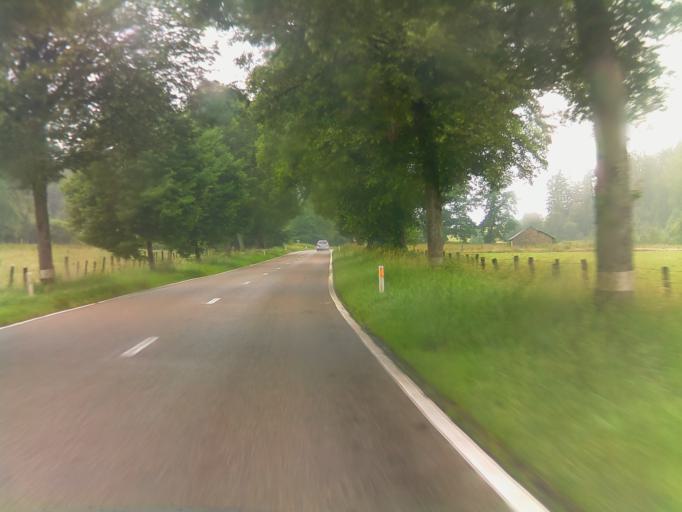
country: BE
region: Wallonia
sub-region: Province du Luxembourg
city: Neufchateau
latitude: 49.8431
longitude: 5.3599
